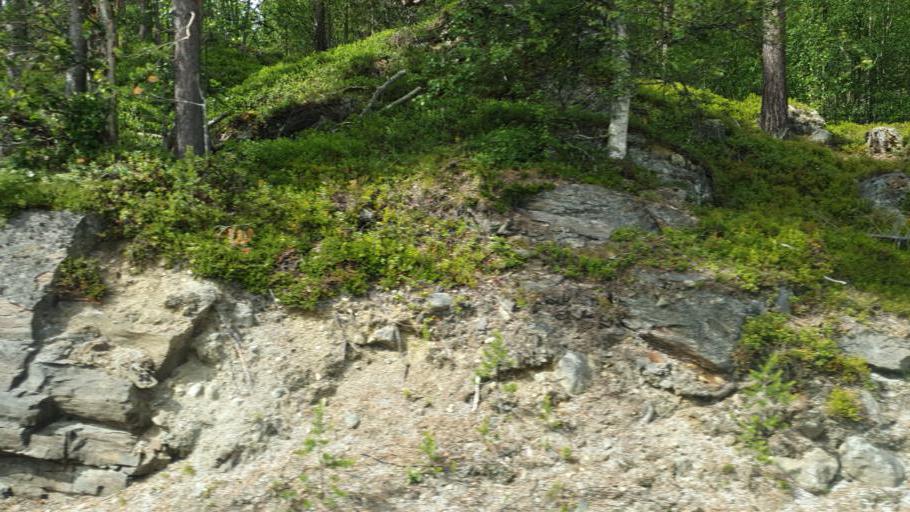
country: NO
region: Oppland
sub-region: Vaga
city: Vagamo
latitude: 61.7404
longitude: 9.0915
